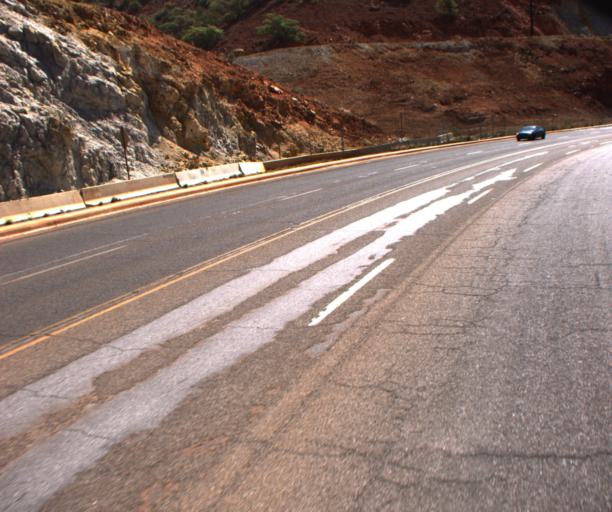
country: US
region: Arizona
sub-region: Cochise County
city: Bisbee
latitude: 31.4402
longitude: -109.9094
